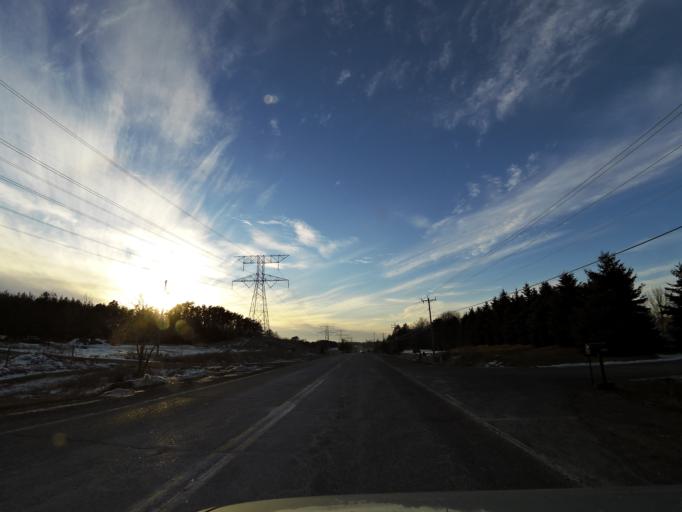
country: US
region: Minnesota
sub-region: Washington County
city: Lake Elmo
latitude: 44.9469
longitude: -92.8351
